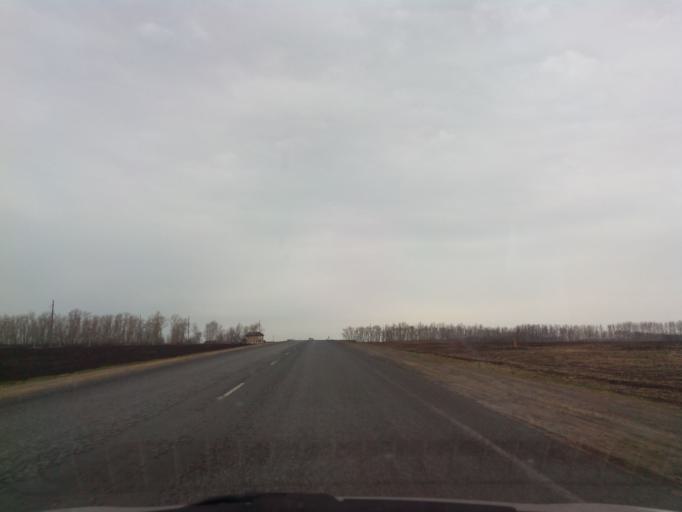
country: RU
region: Tambov
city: Zavoronezhskoye
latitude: 52.9835
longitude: 40.5622
